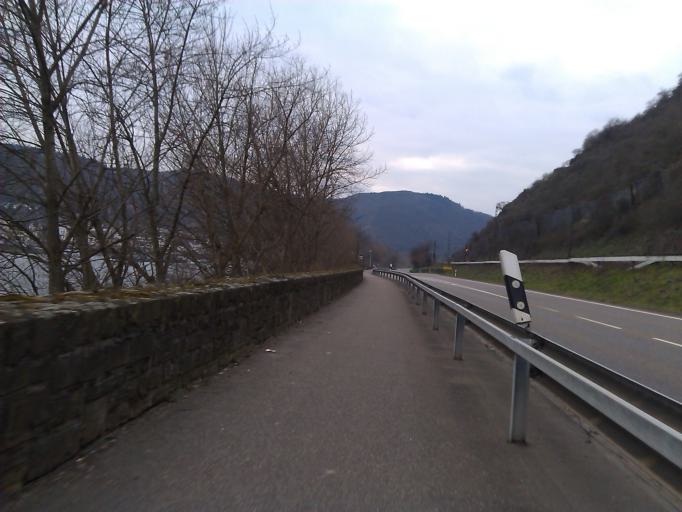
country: DE
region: Rheinland-Pfalz
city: Boppard
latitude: 50.2352
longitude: 7.5959
